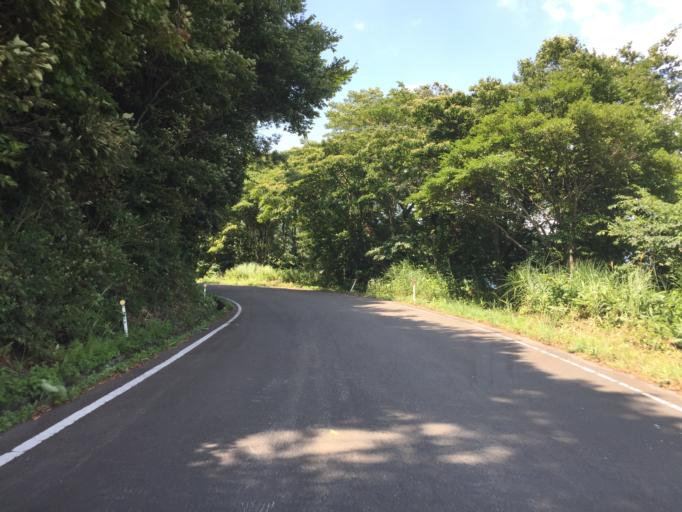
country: JP
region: Fukushima
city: Inawashiro
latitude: 37.4971
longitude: 140.0257
